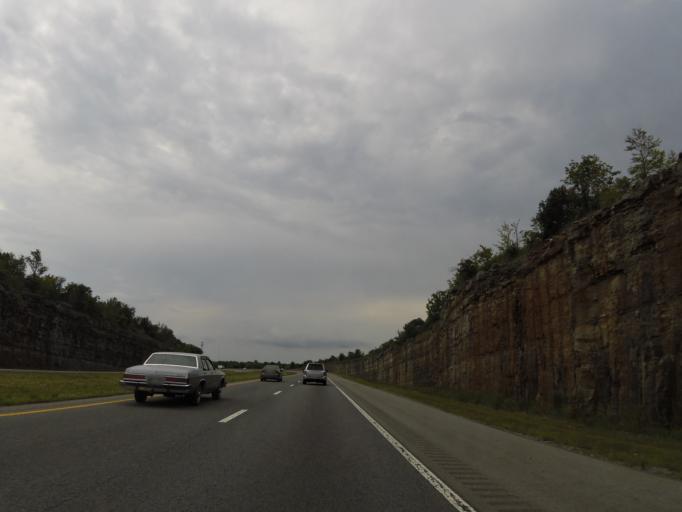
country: US
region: Tennessee
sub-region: Rutherford County
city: Smyrna
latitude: 35.9727
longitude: -86.4473
